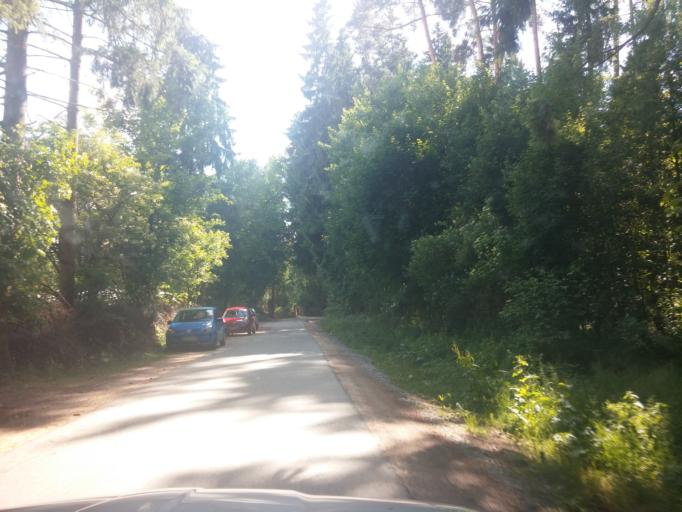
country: DE
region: Bavaria
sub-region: Swabia
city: Illertissen
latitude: 48.2399
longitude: 10.1302
